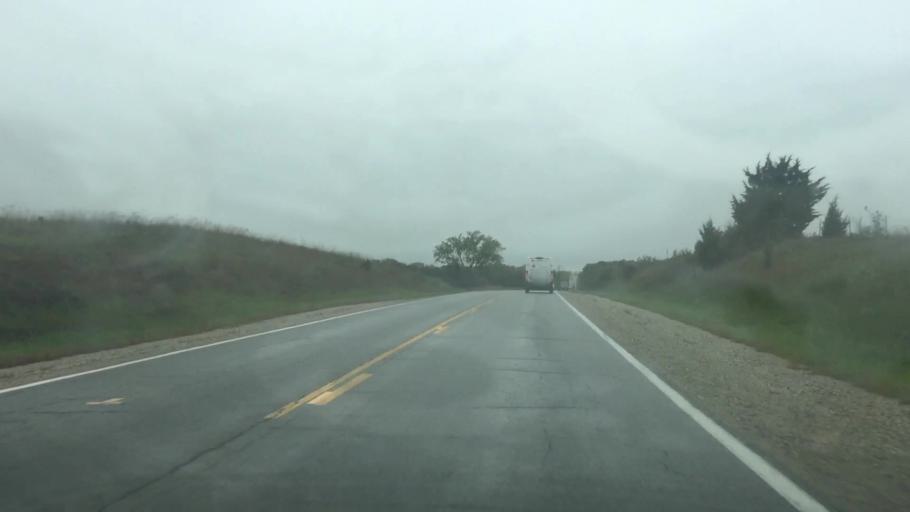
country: US
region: Kansas
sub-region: Anderson County
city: Garnett
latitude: 38.2397
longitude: -95.2480
